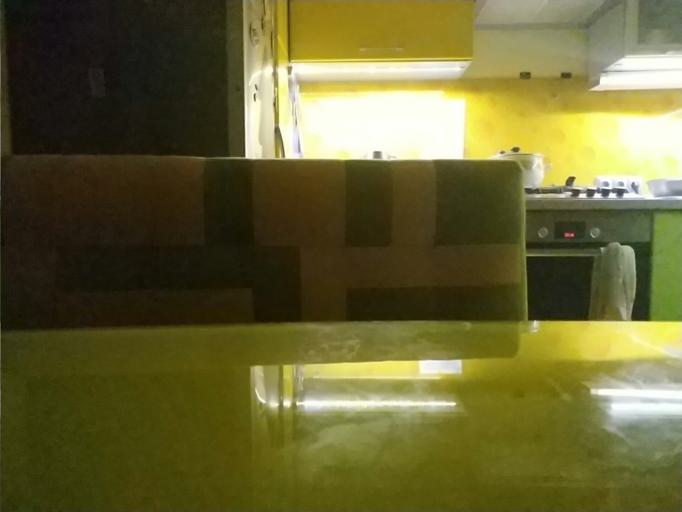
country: RU
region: Republic of Karelia
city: Pyaozerskiy
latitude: 65.4516
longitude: 30.6322
